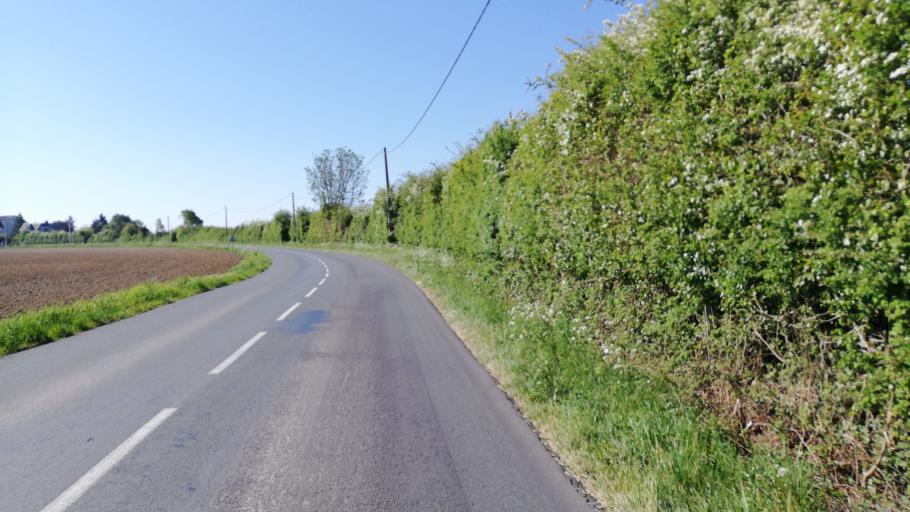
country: FR
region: Pays de la Loire
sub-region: Departement de la Vendee
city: Maillezais
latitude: 46.3291
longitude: -0.7438
